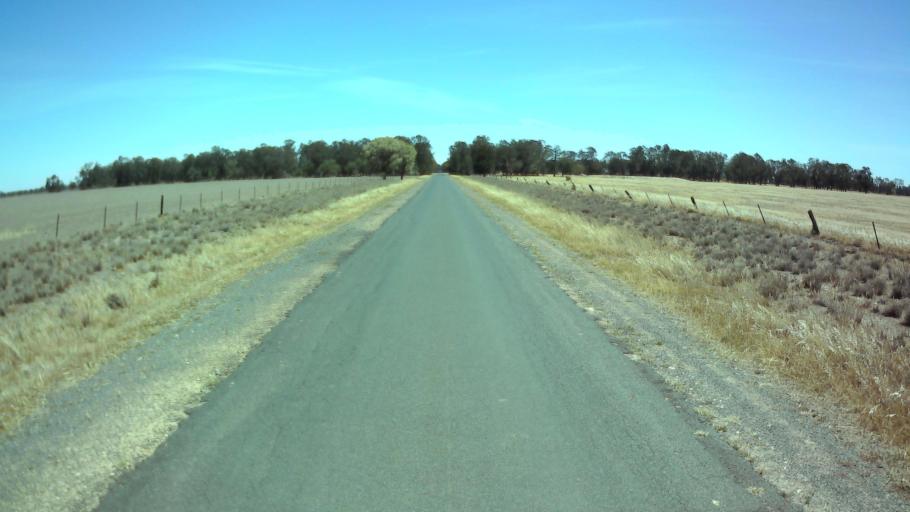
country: AU
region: New South Wales
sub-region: Weddin
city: Grenfell
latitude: -33.8648
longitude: 147.6930
